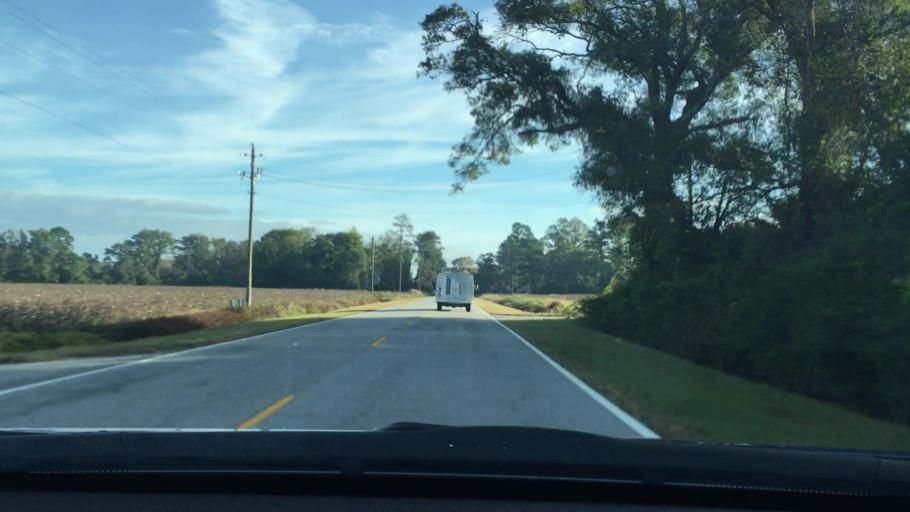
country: US
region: South Carolina
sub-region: Lee County
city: Bishopville
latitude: 34.0989
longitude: -80.1712
